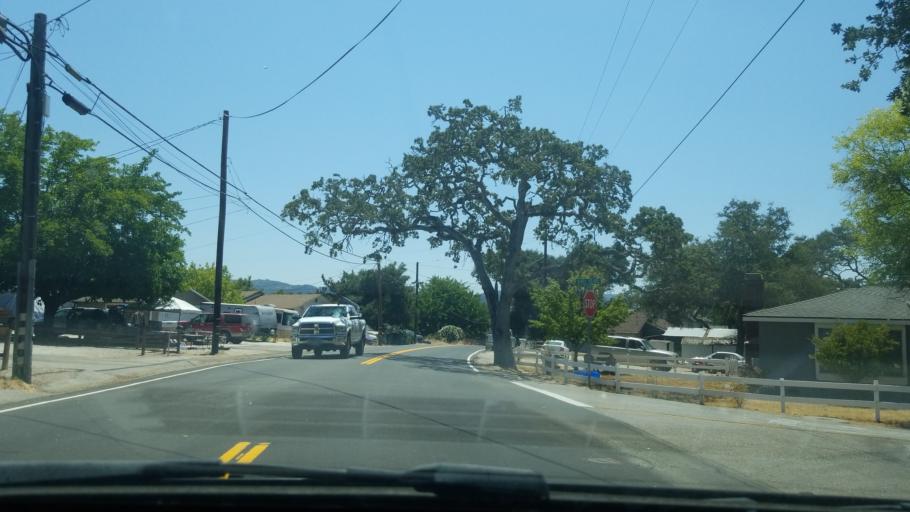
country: US
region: California
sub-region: San Luis Obispo County
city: Atascadero
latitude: 35.4794
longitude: -120.6543
